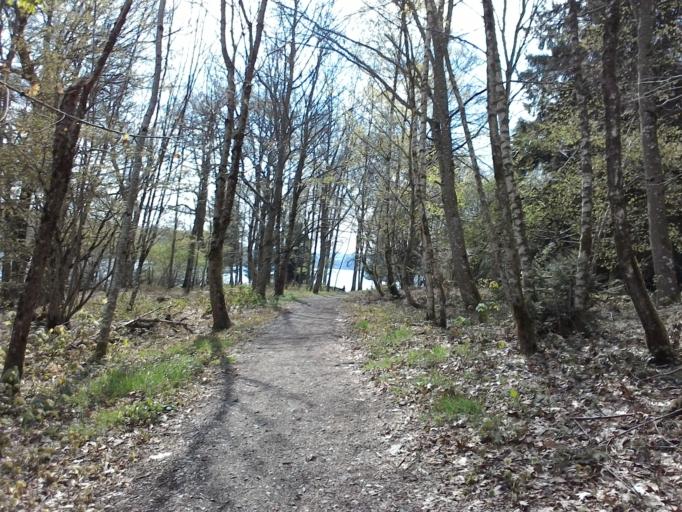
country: FR
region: Bourgogne
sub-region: Departement de la Cote-d'Or
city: Saulieu
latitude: 47.1806
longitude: 4.0803
